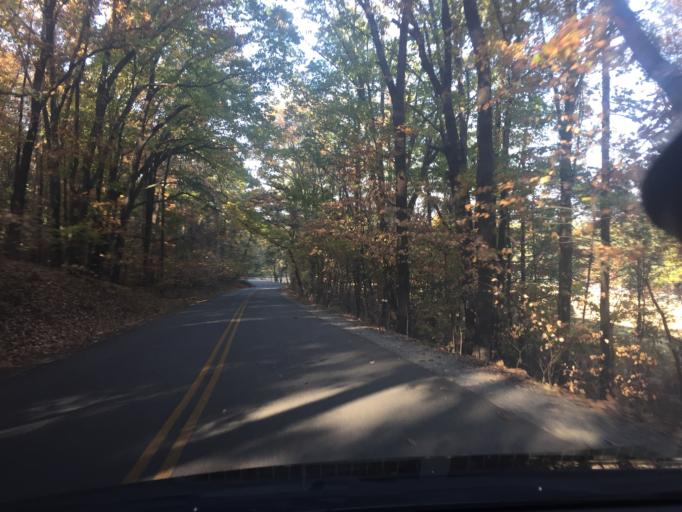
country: US
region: Georgia
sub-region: Cobb County
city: Marietta
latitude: 33.9826
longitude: -84.5747
